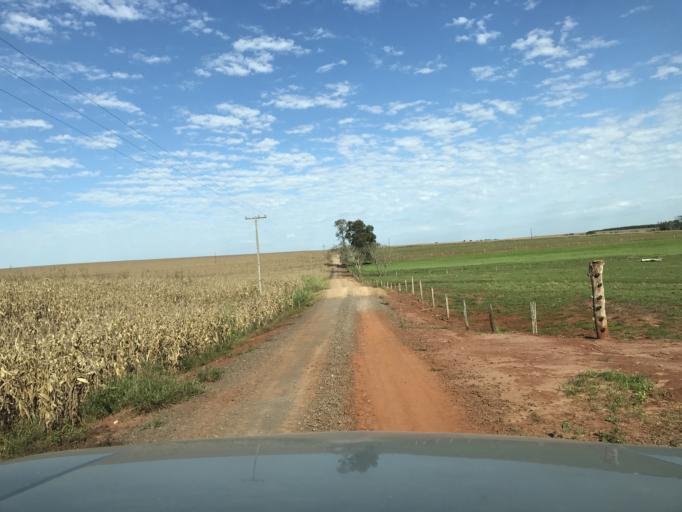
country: BR
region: Parana
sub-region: Palotina
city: Palotina
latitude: -24.1656
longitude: -53.7518
